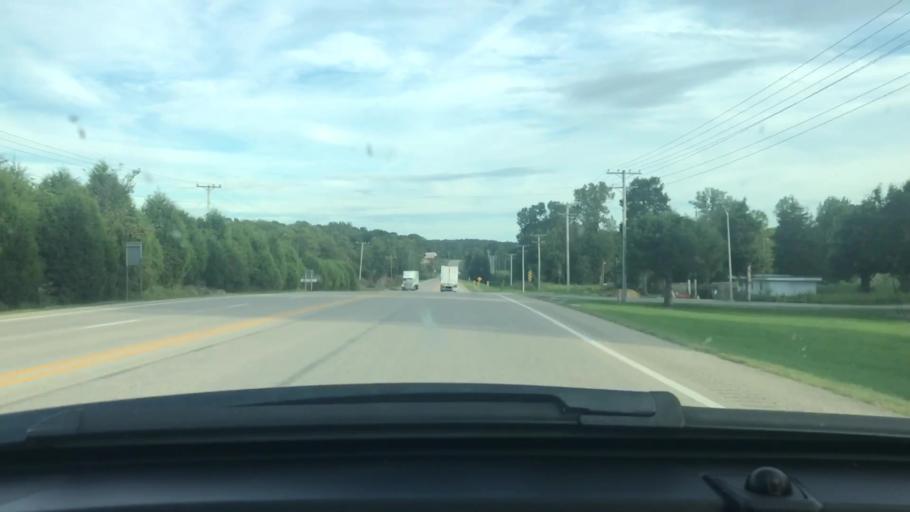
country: US
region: Arkansas
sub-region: Lawrence County
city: Hoxie
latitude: 36.1233
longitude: -91.1518
